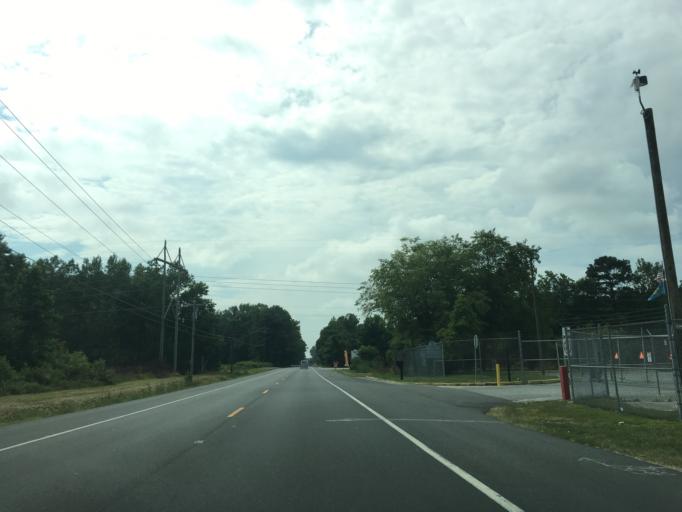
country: US
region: Delaware
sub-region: Sussex County
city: Millsboro
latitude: 38.5597
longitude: -75.2637
